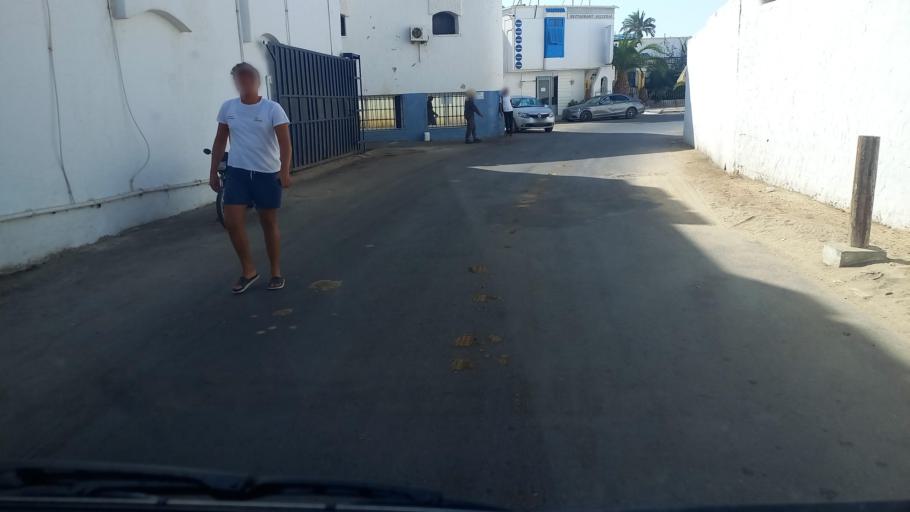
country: TN
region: Madanin
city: Midoun
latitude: 33.8491
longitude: 10.9884
